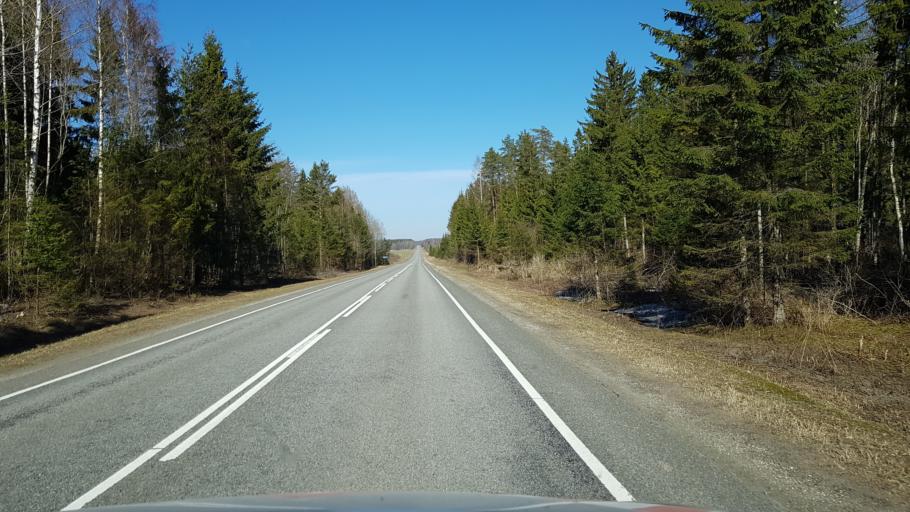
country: EE
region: Laeaene-Virumaa
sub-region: Tamsalu vald
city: Tamsalu
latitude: 59.1264
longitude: 26.0347
